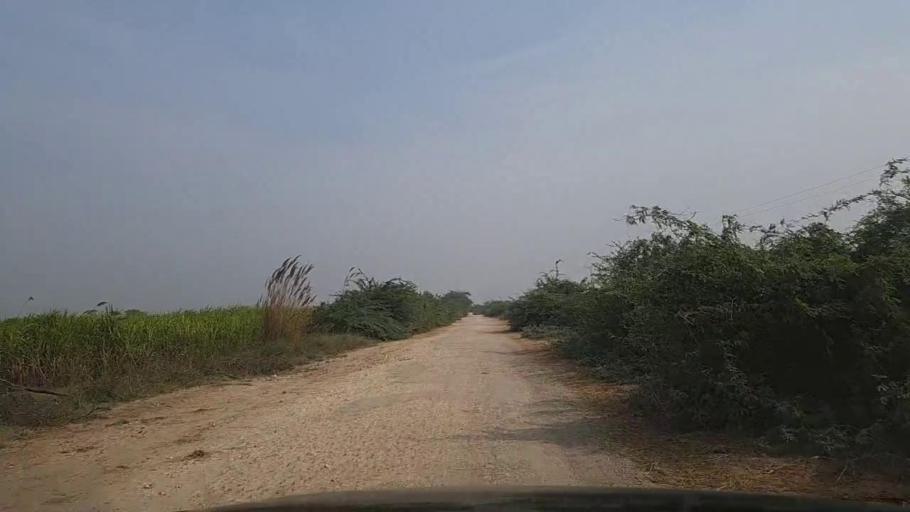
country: PK
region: Sindh
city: Mirpur Sakro
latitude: 24.4024
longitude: 67.7458
